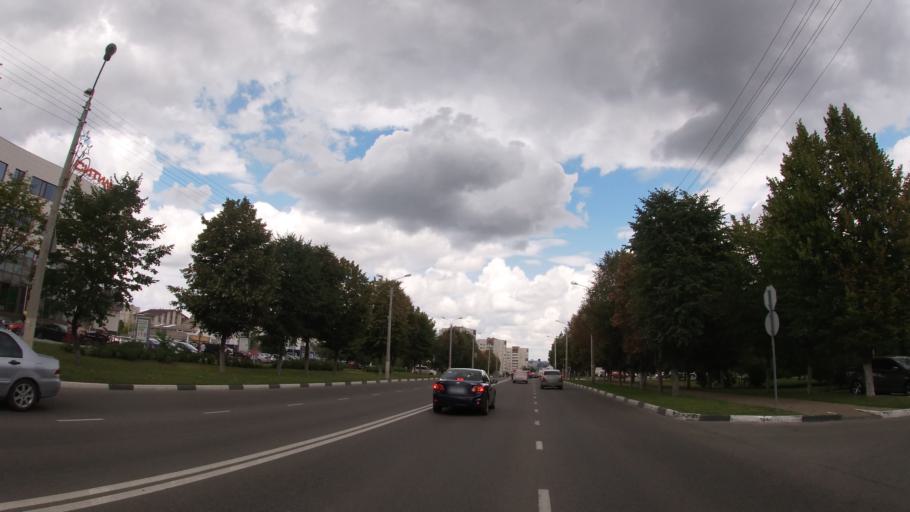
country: RU
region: Belgorod
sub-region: Belgorodskiy Rayon
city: Belgorod
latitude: 50.5765
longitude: 36.5829
